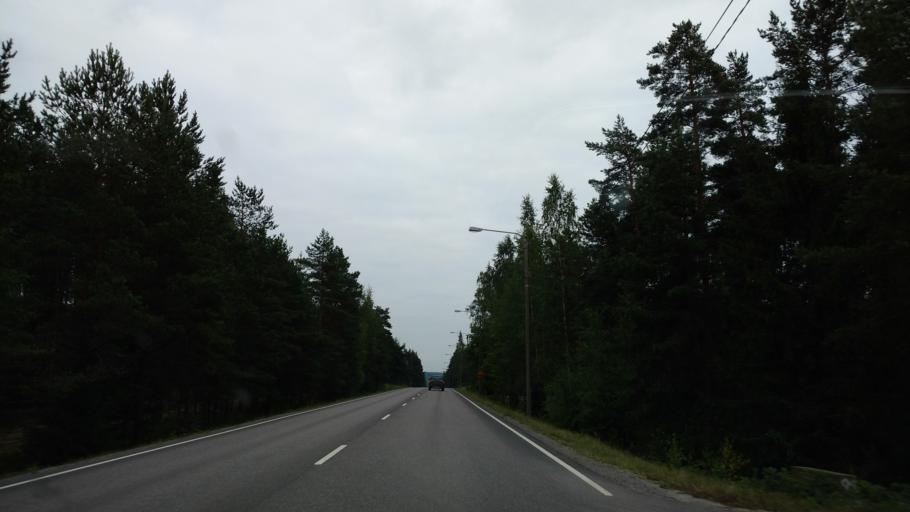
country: FI
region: Varsinais-Suomi
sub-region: Salo
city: Halikko
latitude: 60.4413
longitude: 23.0391
